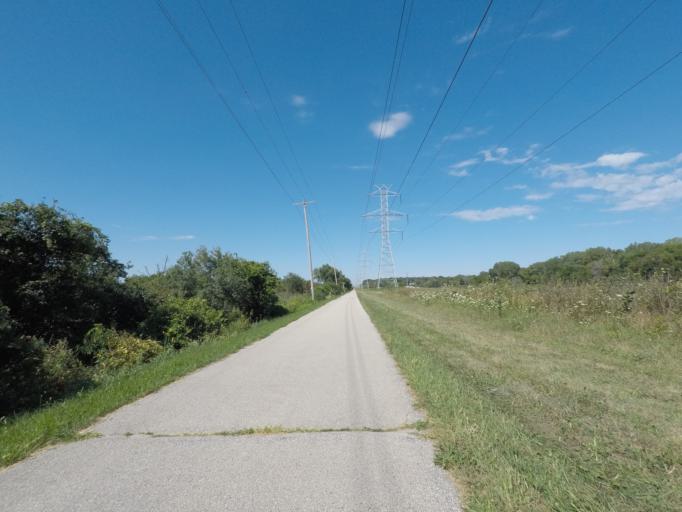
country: US
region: Wisconsin
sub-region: Waukesha County
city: New Berlin
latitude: 43.0100
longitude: -88.1530
